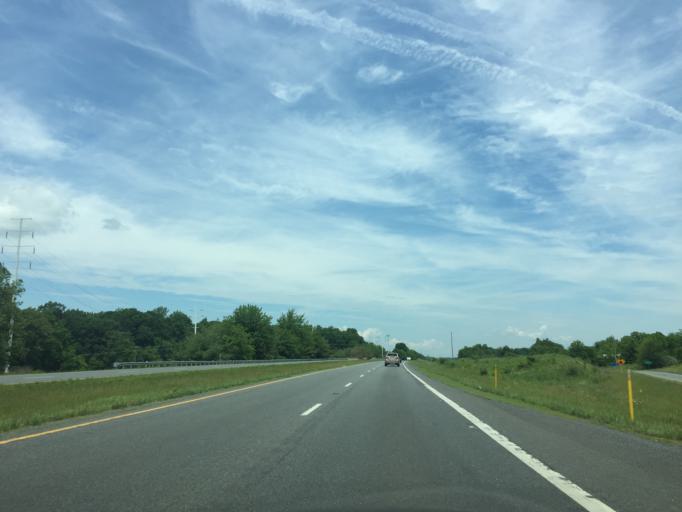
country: US
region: Virginia
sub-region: City of Winchester
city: Winchester
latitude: 39.1561
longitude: -78.2112
